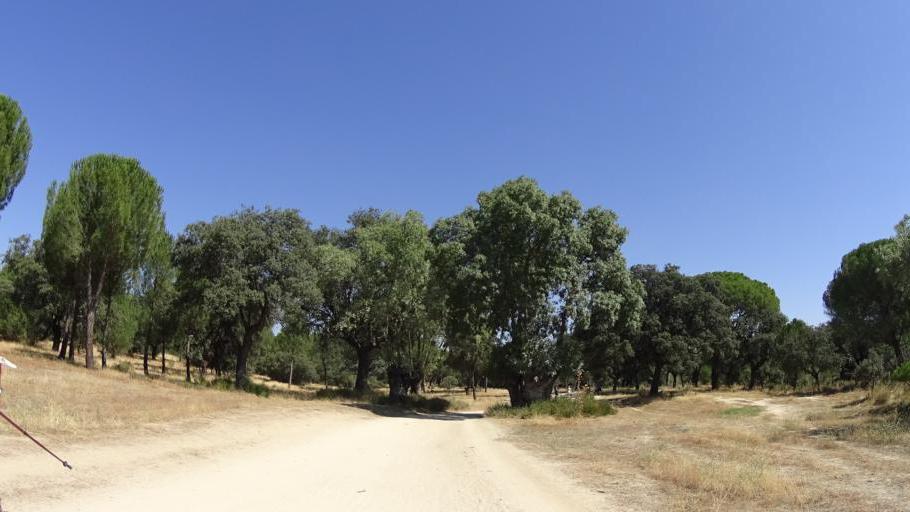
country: ES
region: Madrid
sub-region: Provincia de Madrid
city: Boadilla del Monte
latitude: 40.4225
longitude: -3.8551
